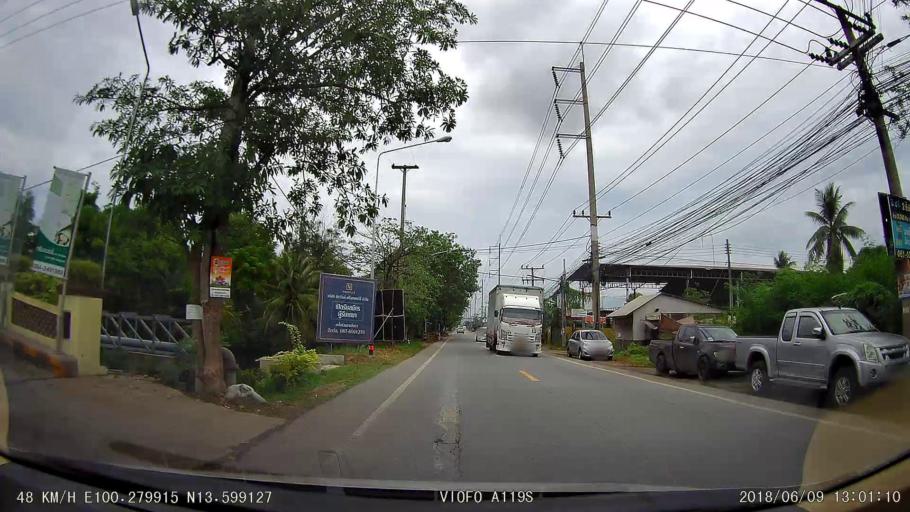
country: TH
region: Samut Sakhon
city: Samut Sakhon
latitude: 13.5991
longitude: 100.2797
